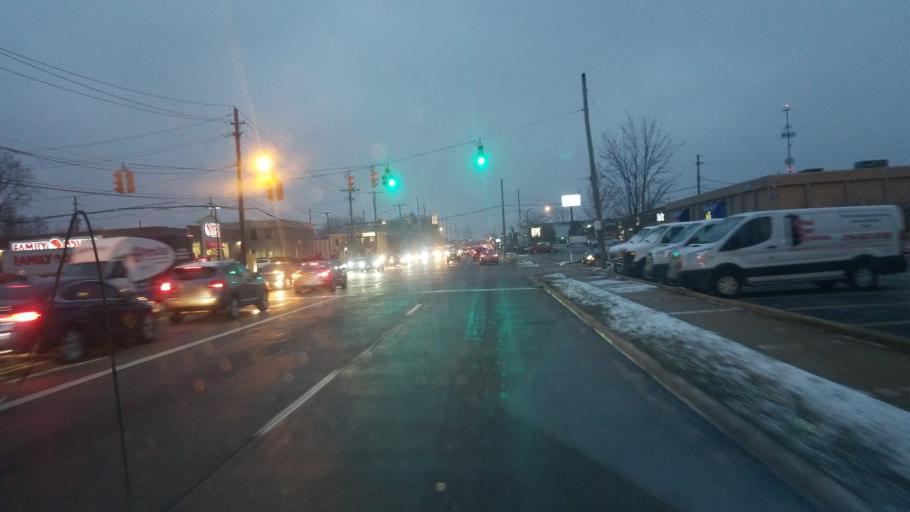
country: US
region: Ohio
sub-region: Cuyahoga County
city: Bedford Heights
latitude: 41.4242
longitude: -81.5176
